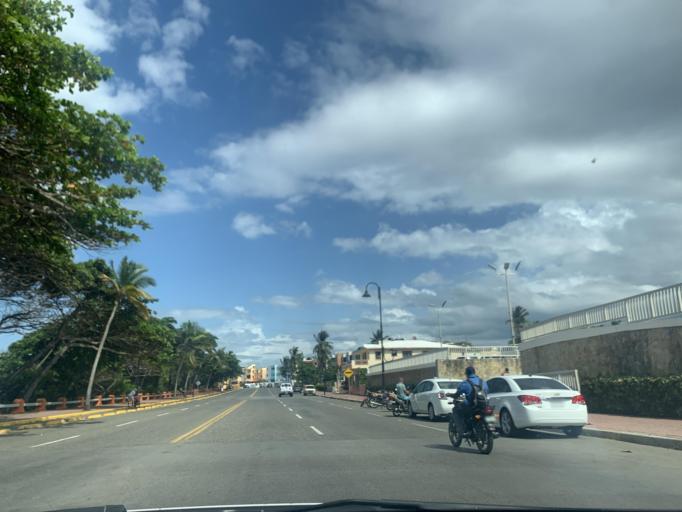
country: DO
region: Puerto Plata
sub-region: Puerto Plata
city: Puerto Plata
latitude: 19.7961
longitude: -70.6844
